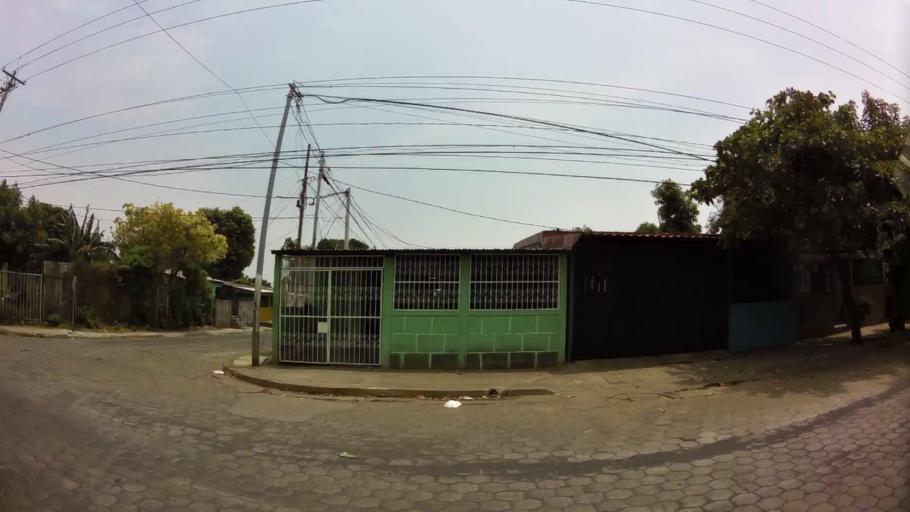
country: NI
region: Managua
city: Managua
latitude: 12.1451
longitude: -86.2959
